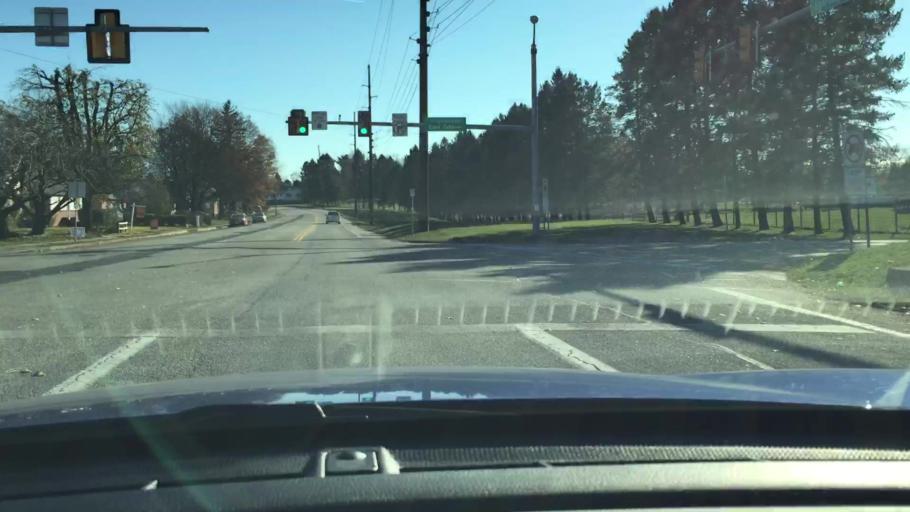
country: US
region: Pennsylvania
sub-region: Cumberland County
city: Shiremanstown
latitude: 40.2299
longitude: -76.9714
